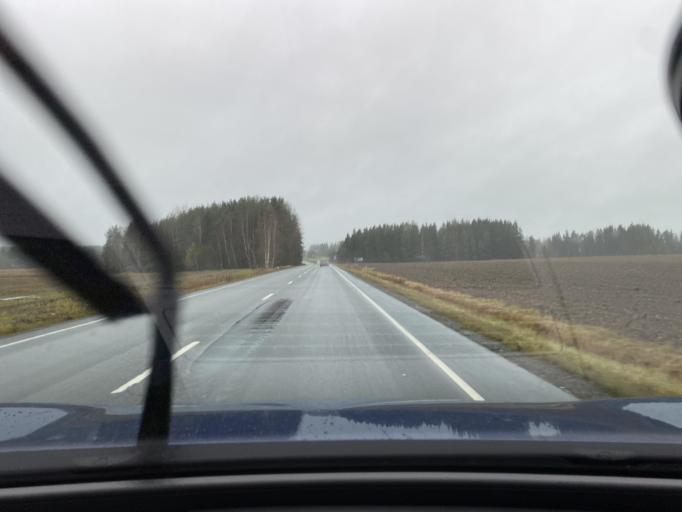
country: FI
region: Varsinais-Suomi
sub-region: Loimaa
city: Alastaro
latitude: 60.9305
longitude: 22.8777
